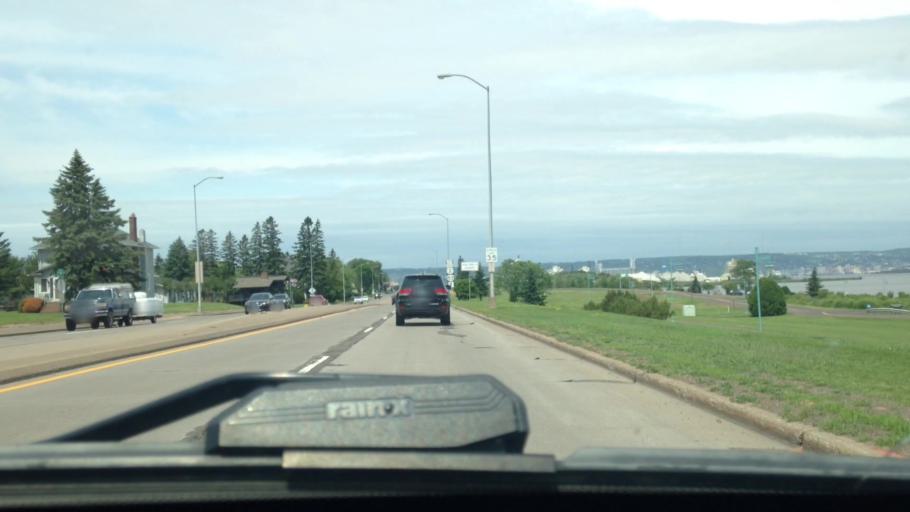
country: US
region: Wisconsin
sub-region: Douglas County
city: Superior
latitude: 46.7190
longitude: -92.0635
